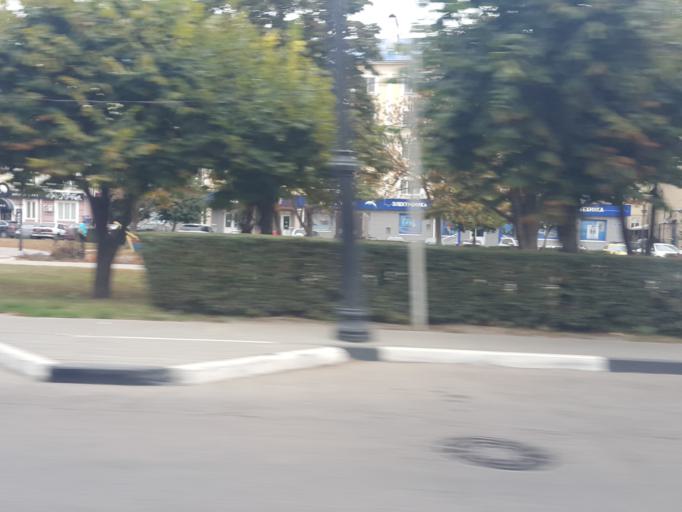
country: RU
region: Tambov
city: Tambov
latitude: 52.7265
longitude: 41.4507
